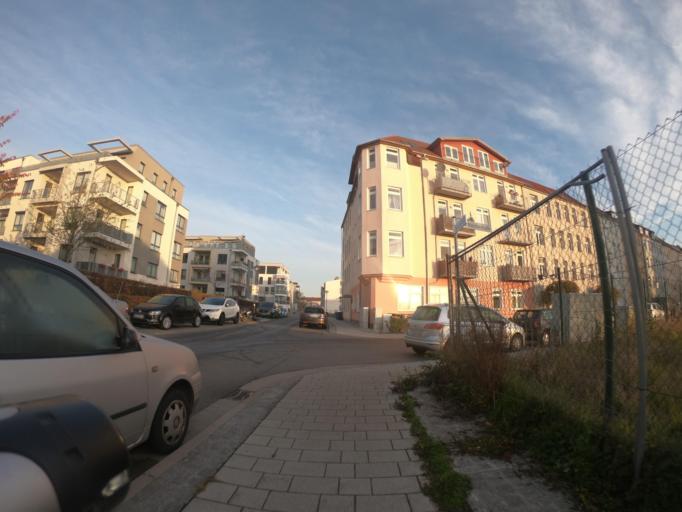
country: DE
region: Mecklenburg-Vorpommern
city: Rostock
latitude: 54.0842
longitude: 12.1462
